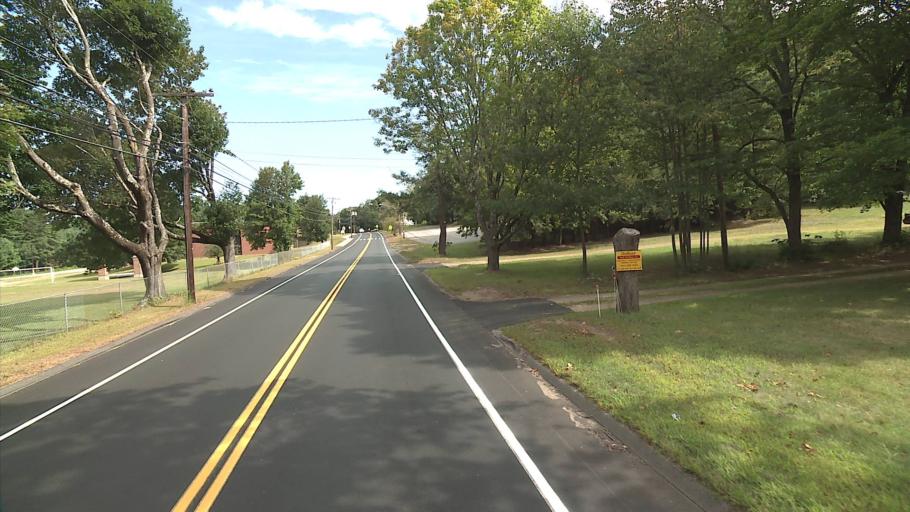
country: US
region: Connecticut
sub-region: Tolland County
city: Storrs
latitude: 41.8500
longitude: -72.3025
